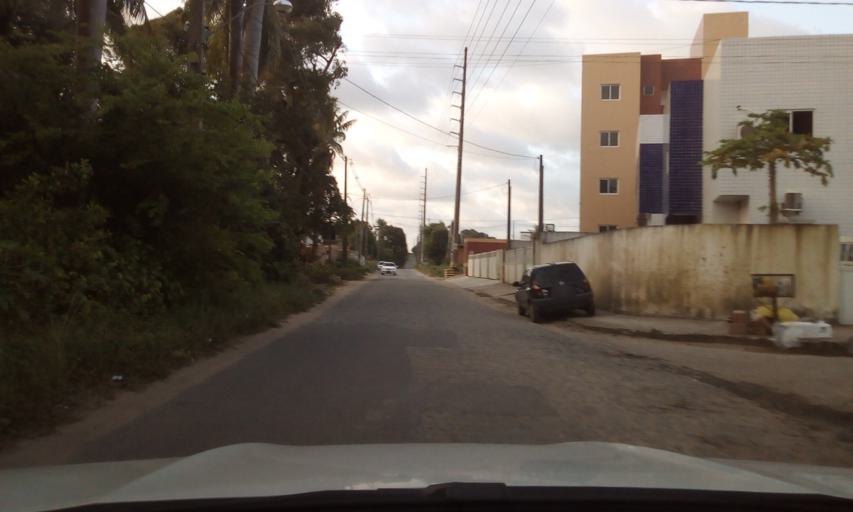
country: BR
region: Paraiba
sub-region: Bayeux
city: Bayeux
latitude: -7.1870
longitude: -34.8915
